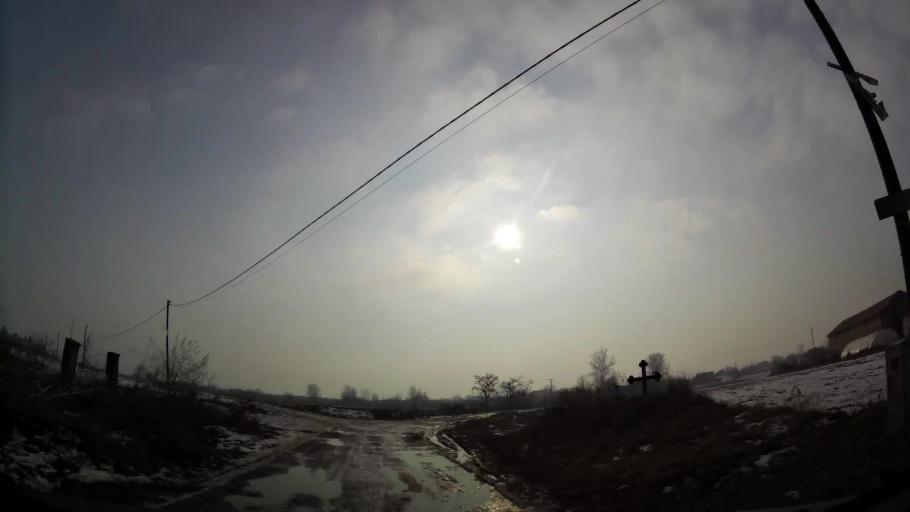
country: MK
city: Kadino
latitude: 41.9711
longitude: 21.6052
